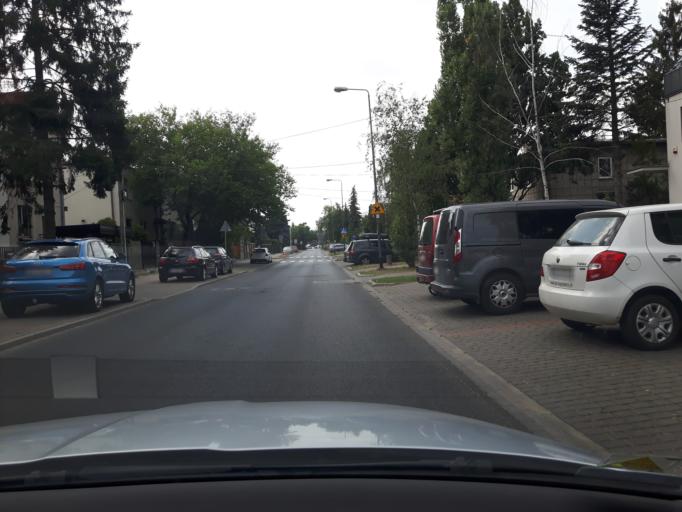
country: PL
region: Masovian Voivodeship
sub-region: Warszawa
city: Mokotow
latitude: 52.1911
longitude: 21.0666
